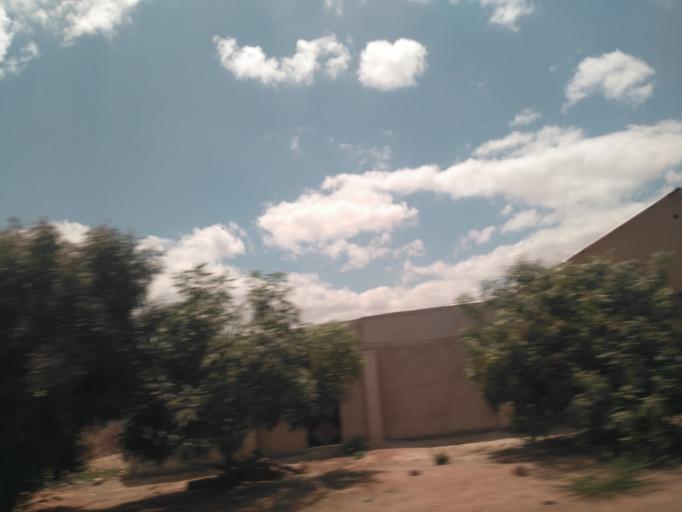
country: TZ
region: Dodoma
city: Kisasa
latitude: -6.1704
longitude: 35.8004
